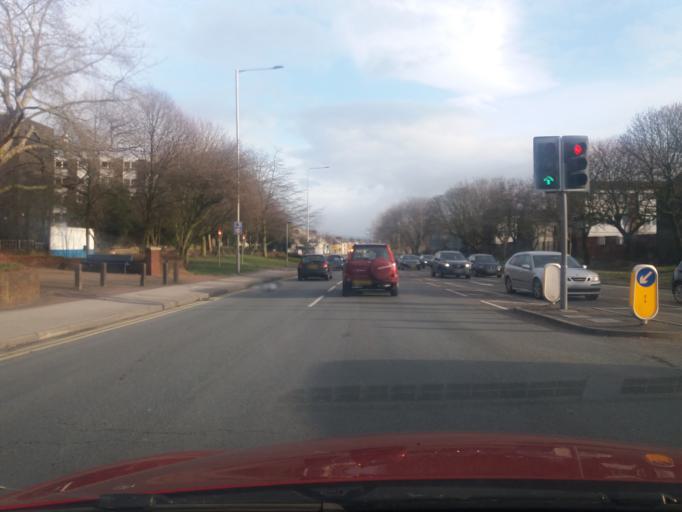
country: GB
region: England
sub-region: Lancashire
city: Preston
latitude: 53.7598
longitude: -2.6863
